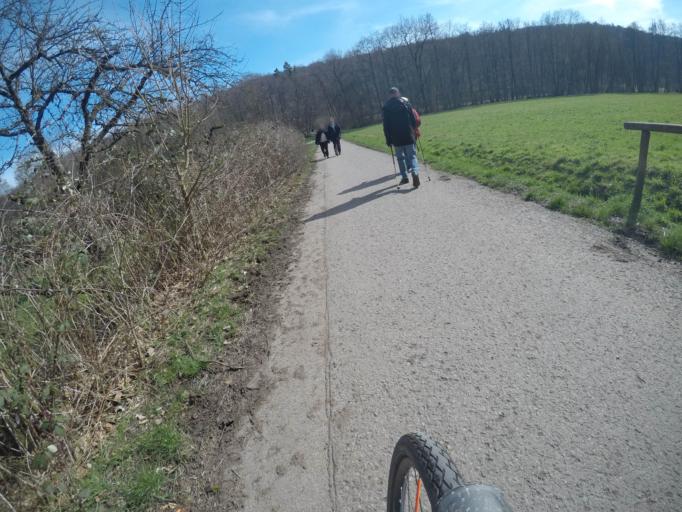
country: DE
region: Baden-Wuerttemberg
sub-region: Regierungsbezirk Stuttgart
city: Korntal
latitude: 48.8027
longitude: 9.1170
